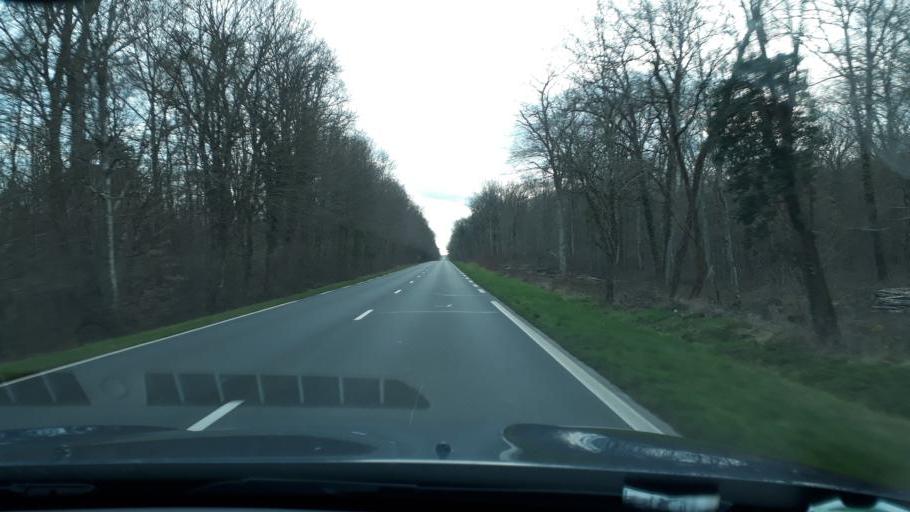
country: FR
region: Centre
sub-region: Departement du Loiret
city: Chilleurs-aux-Bois
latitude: 48.0499
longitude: 2.1269
